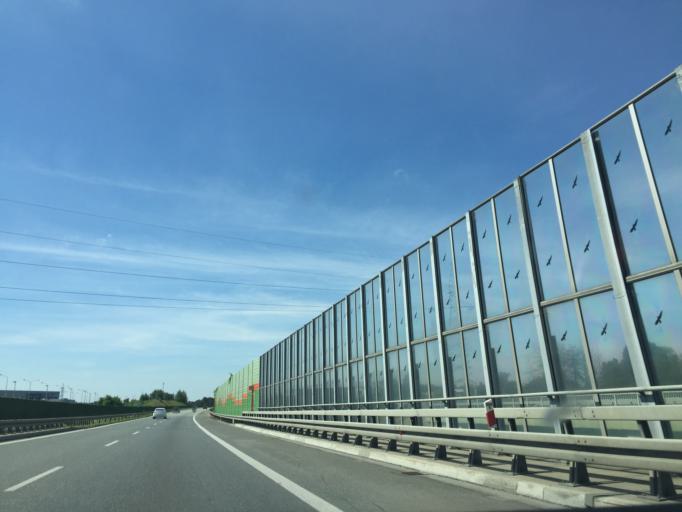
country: PL
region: Lodz Voivodeship
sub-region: Powiat tomaszowski
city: Tomaszow Mazowiecki
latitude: 51.5546
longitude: 20.0016
